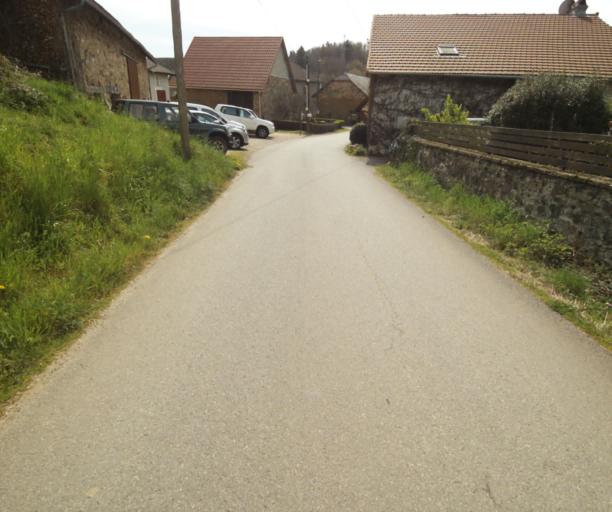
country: FR
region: Limousin
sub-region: Departement de la Correze
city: Naves
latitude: 45.3015
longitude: 1.7640
